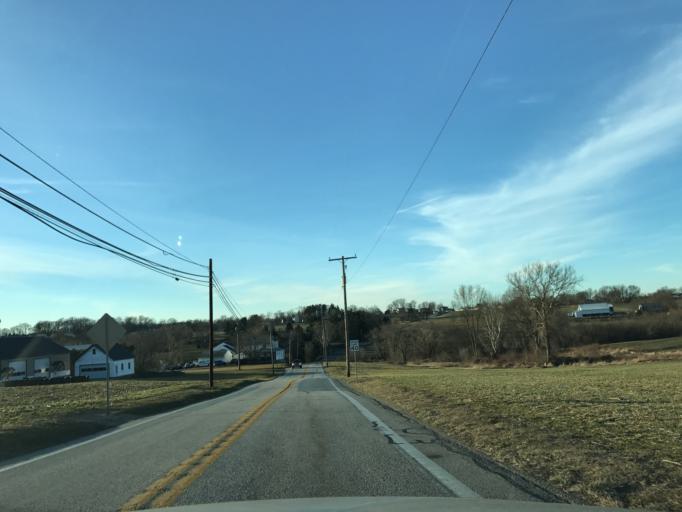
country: US
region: Pennsylvania
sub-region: Lancaster County
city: Elizabethtown
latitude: 40.1292
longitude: -76.5962
